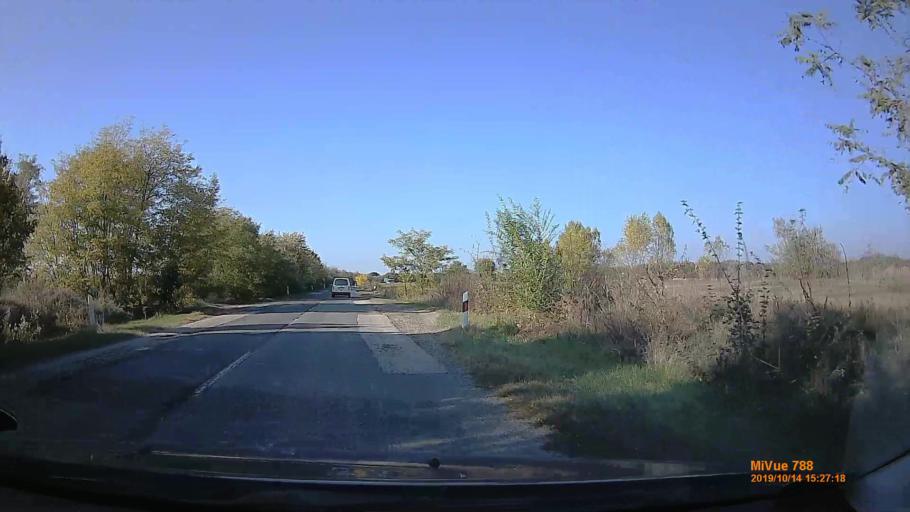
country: HU
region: Pest
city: Ecser
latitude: 47.4286
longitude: 19.3075
